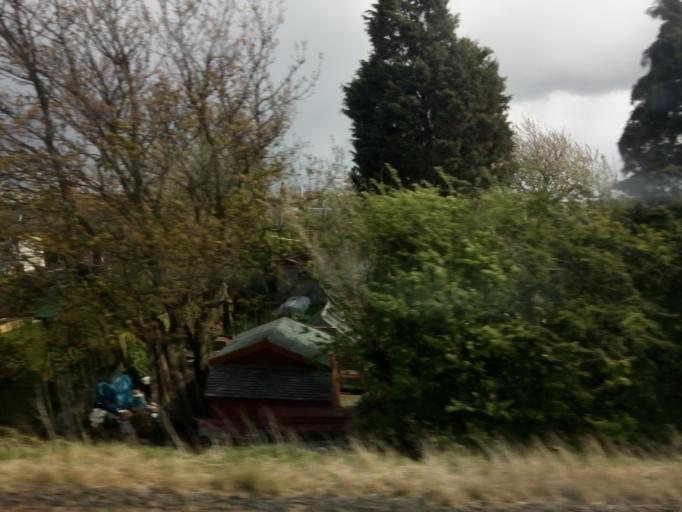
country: GB
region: Scotland
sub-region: East Lothian
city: Gullane
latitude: 55.9935
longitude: -2.8307
